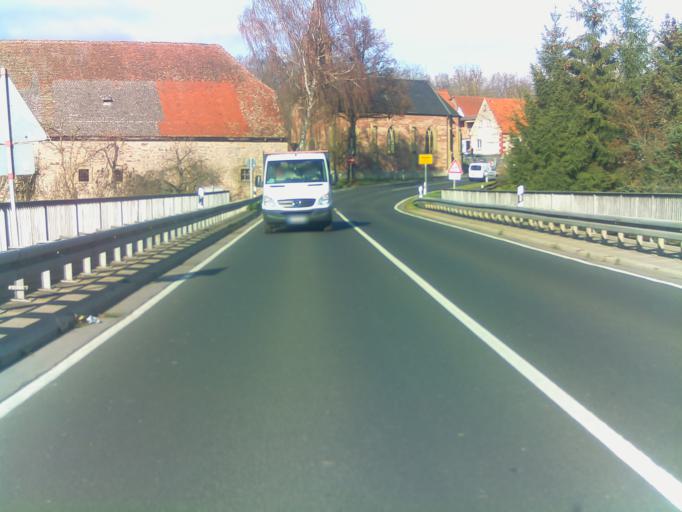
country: DE
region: Bavaria
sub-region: Regierungsbezirk Unterfranken
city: Bad Bocklet
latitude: 50.2361
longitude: 10.0742
